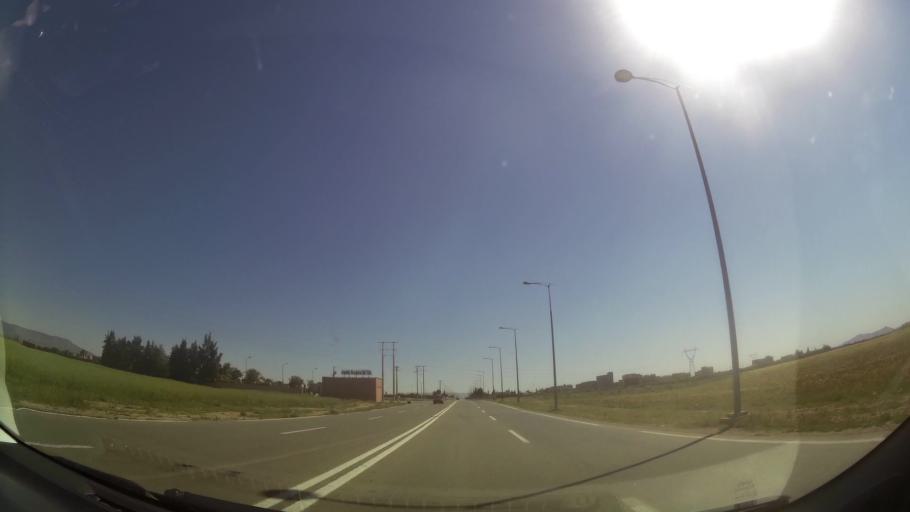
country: MA
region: Oriental
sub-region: Oujda-Angad
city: Oujda
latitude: 34.7268
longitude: -1.8767
